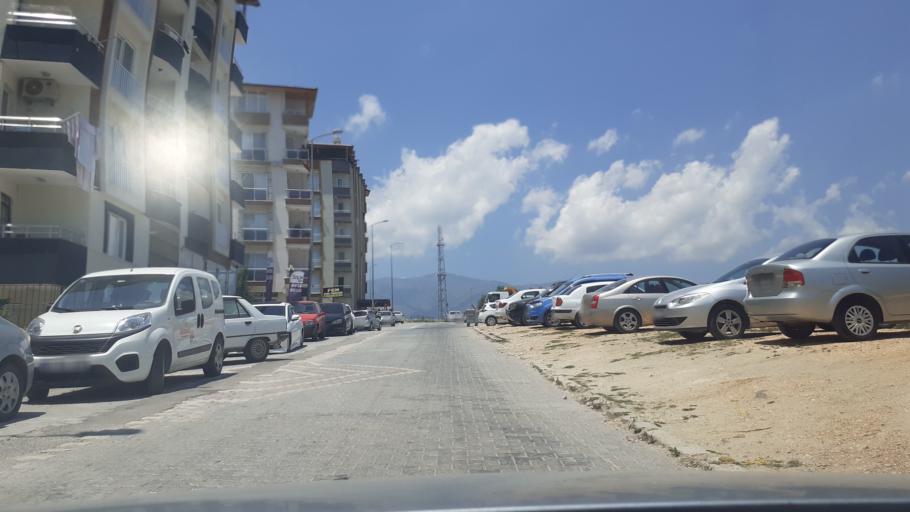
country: TR
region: Hatay
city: Gunyazi
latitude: 36.2339
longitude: 36.1391
